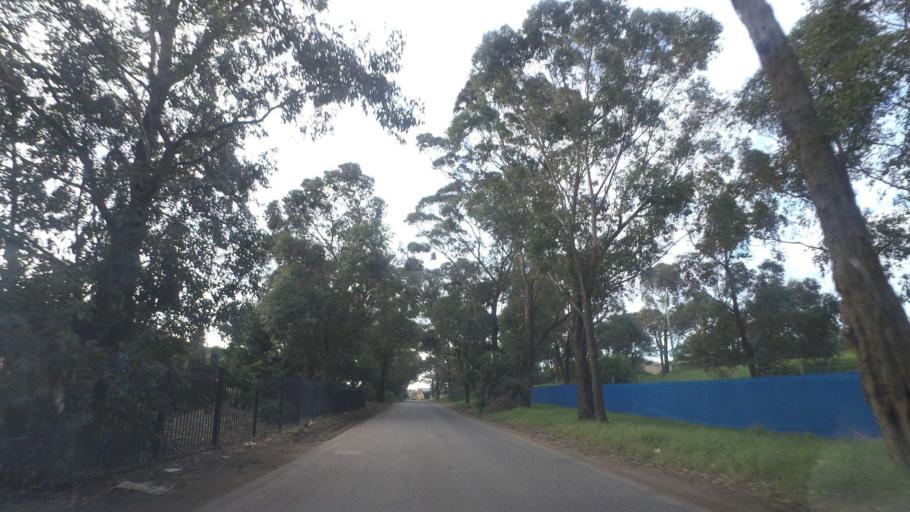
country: AU
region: Victoria
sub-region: Kingston
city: Clayton South
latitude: -37.9452
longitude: 145.1206
